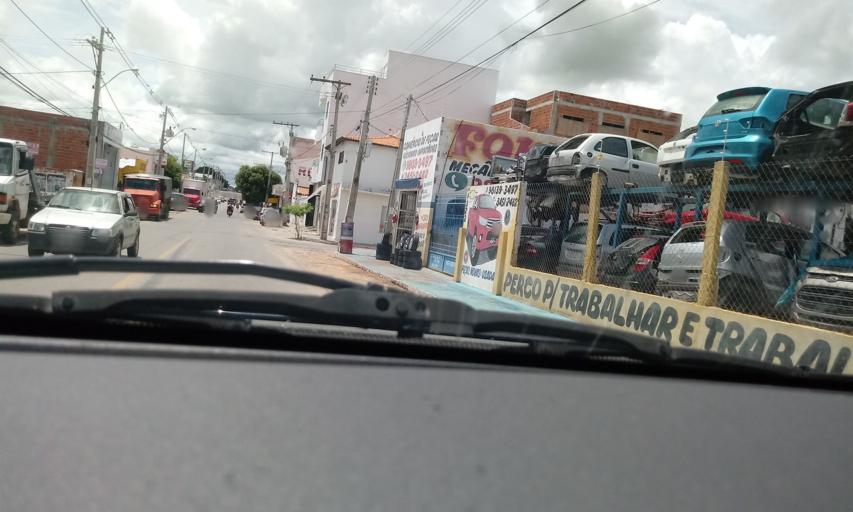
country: BR
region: Bahia
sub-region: Guanambi
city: Guanambi
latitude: -14.2155
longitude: -42.7727
